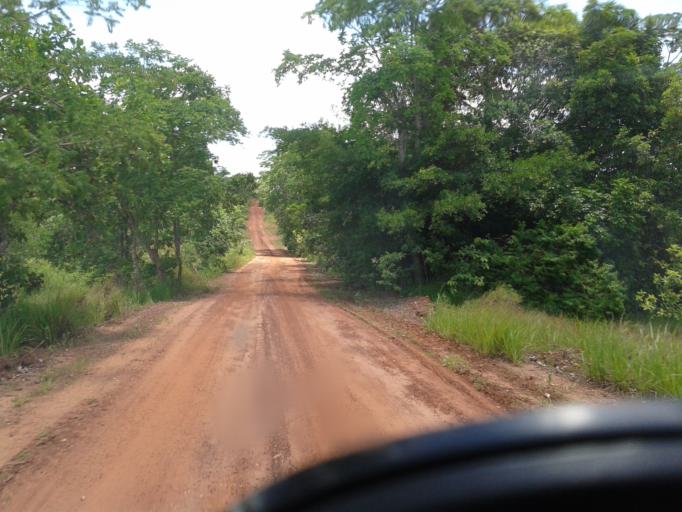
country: BR
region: Minas Gerais
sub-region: Santa Vitoria
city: Santa Vitoria
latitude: -18.9802
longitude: -49.8938
